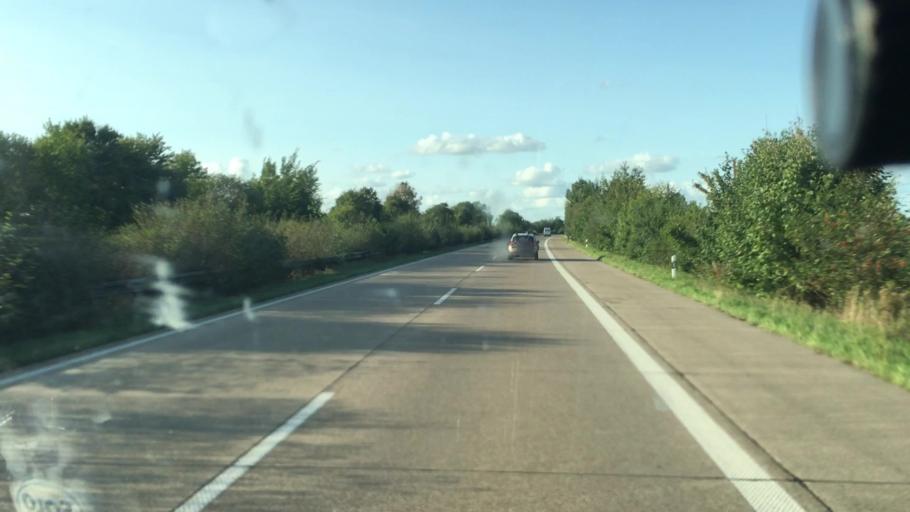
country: DE
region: Lower Saxony
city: Sande
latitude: 53.4564
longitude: 8.0197
